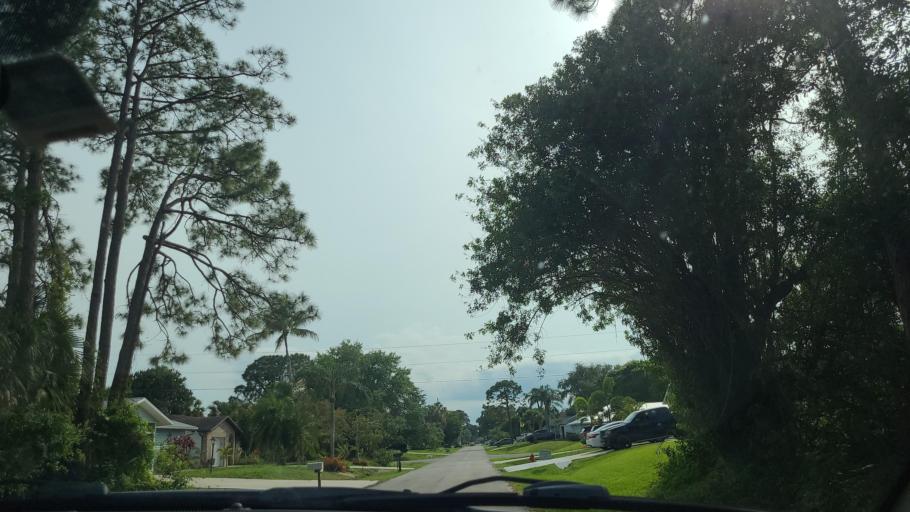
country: US
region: Florida
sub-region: Indian River County
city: Sebastian
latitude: 27.7621
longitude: -80.4783
